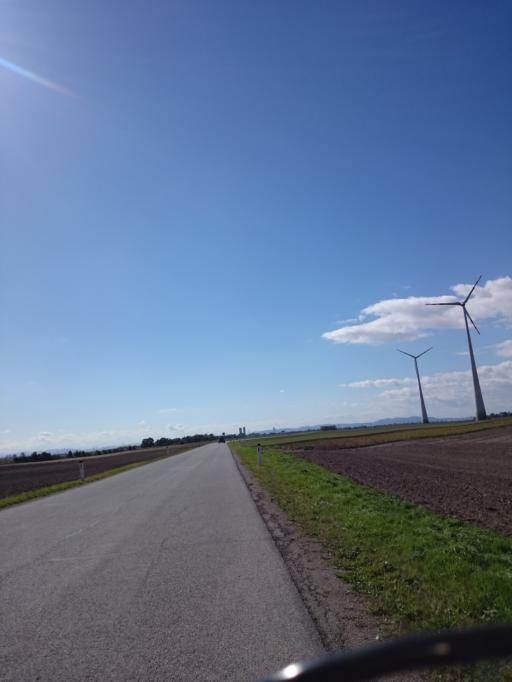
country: AT
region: Lower Austria
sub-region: Politischer Bezirk Ganserndorf
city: Glinzendorf
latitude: 48.2429
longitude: 16.6254
